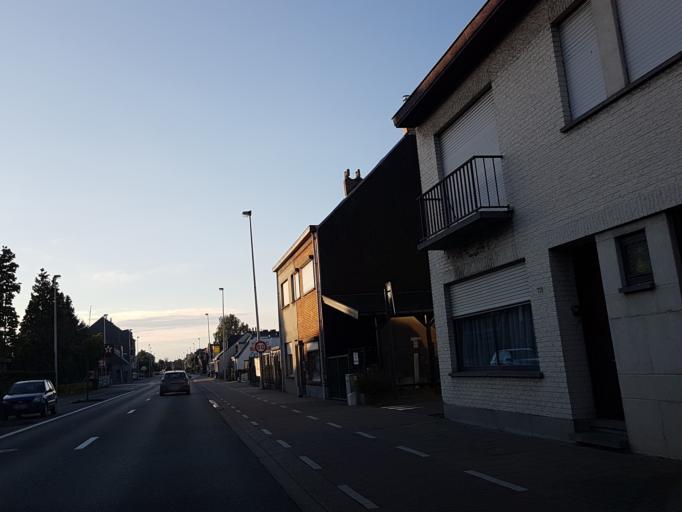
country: BE
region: Flanders
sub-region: Provincie Oost-Vlaanderen
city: Lebbeke
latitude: 51.0106
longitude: 4.1176
